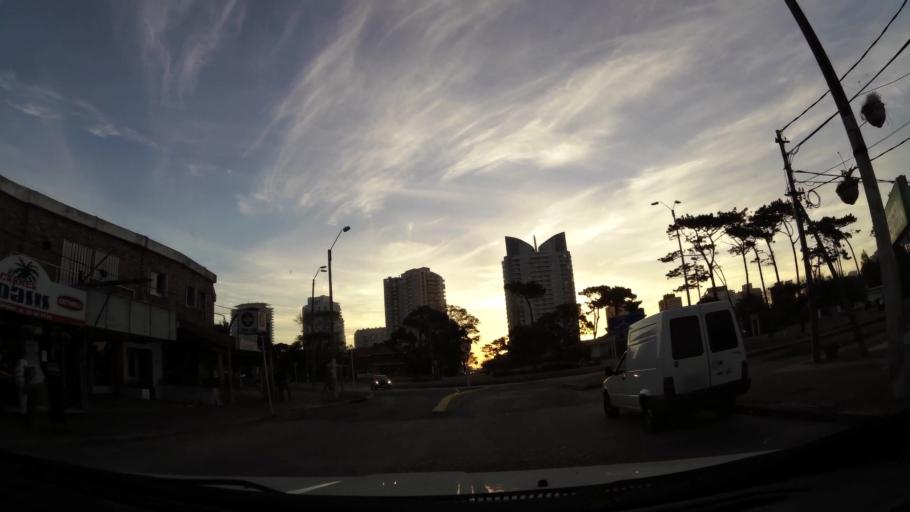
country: UY
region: Maldonado
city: Punta del Este
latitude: -34.9453
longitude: -54.9363
